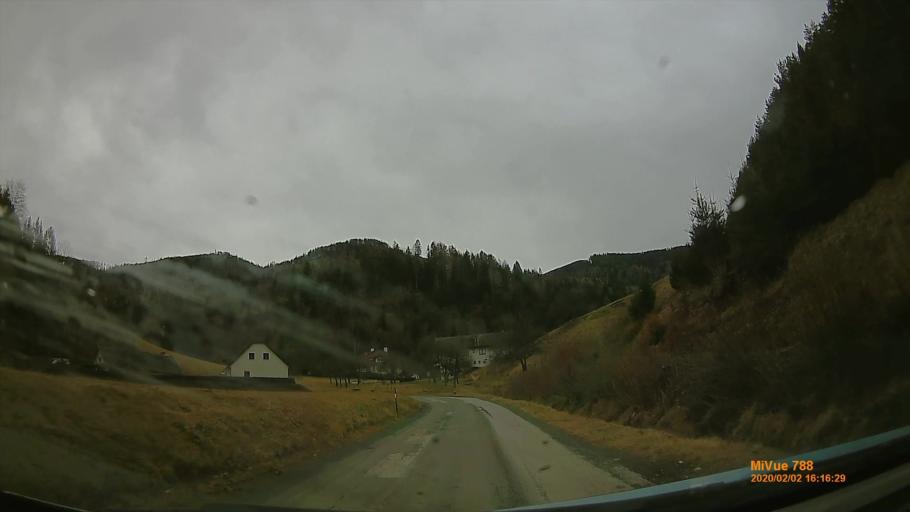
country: AT
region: Lower Austria
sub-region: Politischer Bezirk Neunkirchen
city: Semmering
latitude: 47.6516
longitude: 15.8160
